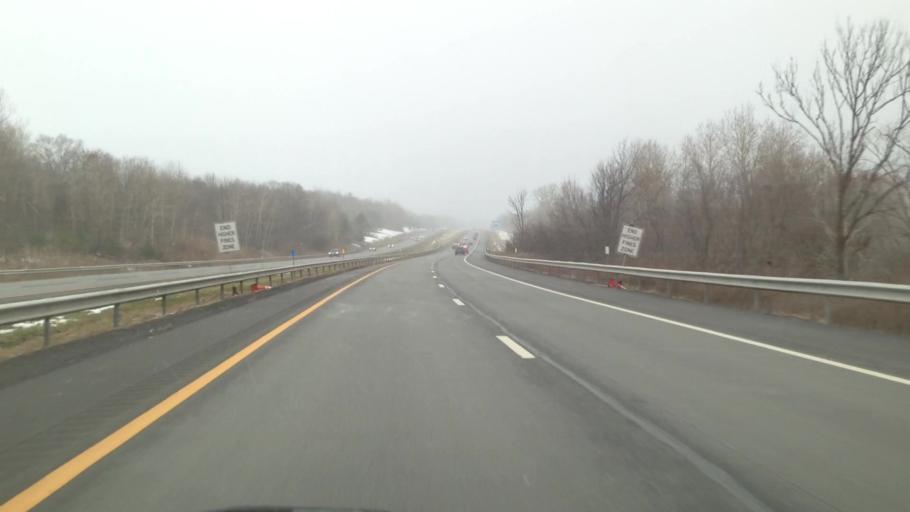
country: US
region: New York
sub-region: Schenectady County
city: Scotia
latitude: 42.8756
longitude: -74.0601
